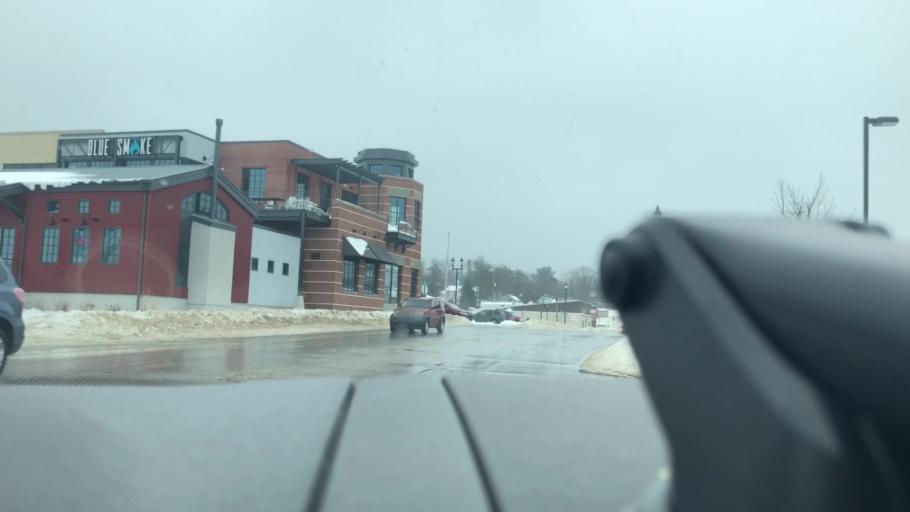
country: US
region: Michigan
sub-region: Charlevoix County
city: East Jordan
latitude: 45.1541
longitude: -85.1284
